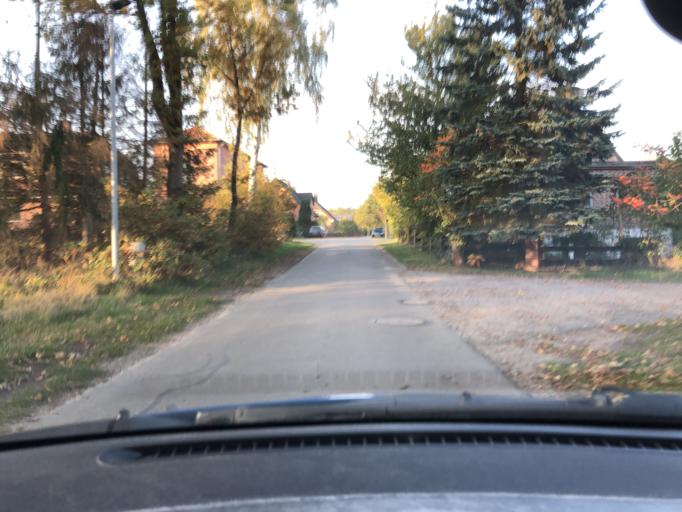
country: DE
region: Lower Saxony
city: Hitzacker
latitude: 53.1499
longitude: 11.0041
